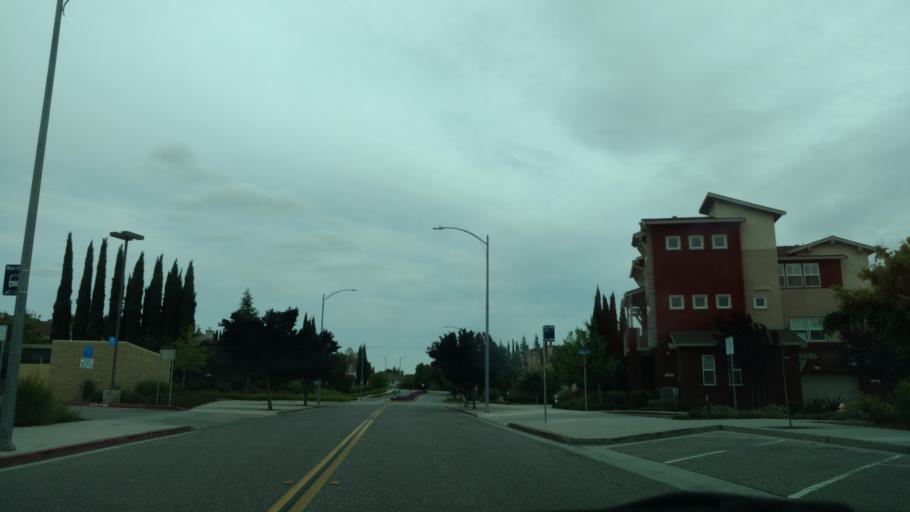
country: US
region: California
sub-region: Santa Clara County
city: Seven Trees
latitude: 37.3132
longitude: -121.7735
